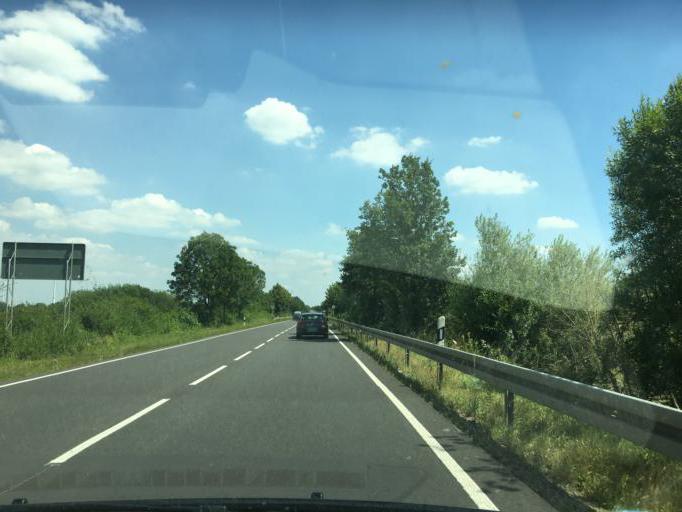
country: DE
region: North Rhine-Westphalia
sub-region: Regierungsbezirk Koln
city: Langerwehe
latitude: 50.8243
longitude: 6.3540
